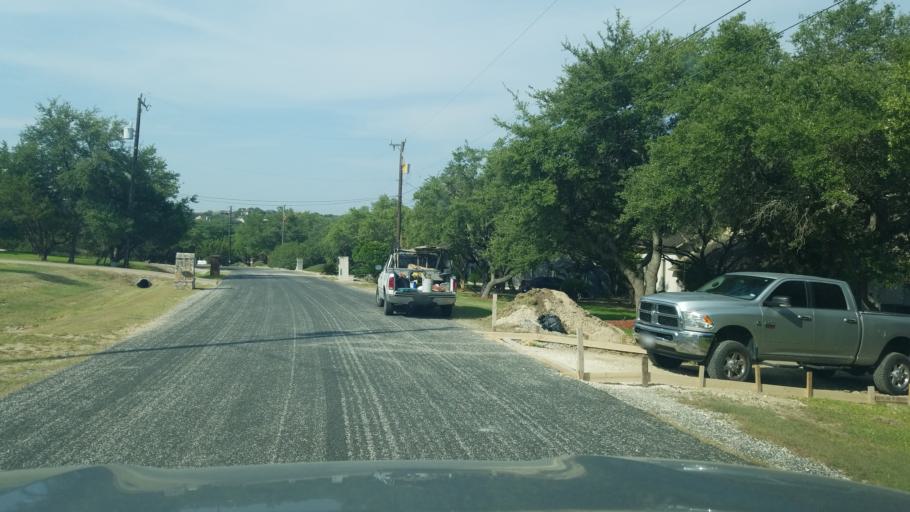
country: US
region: Texas
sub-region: Bexar County
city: Timberwood Park
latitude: 29.6874
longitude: -98.4951
